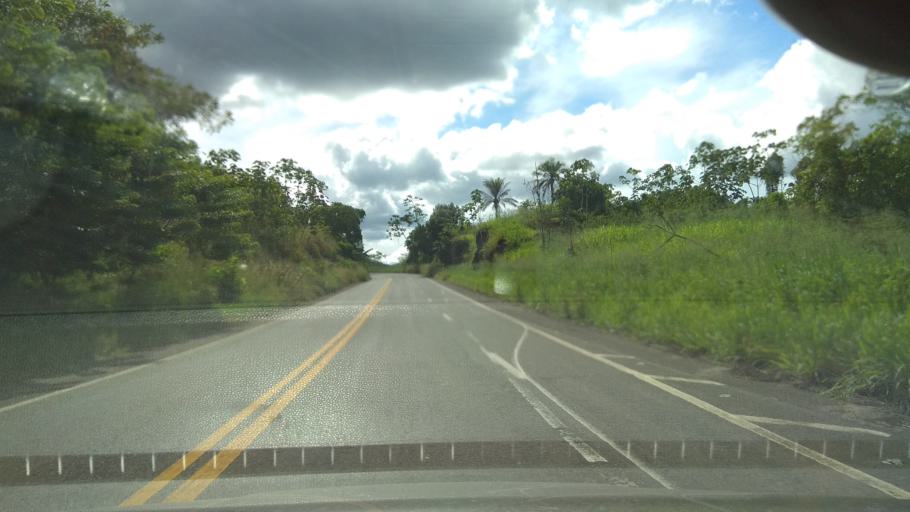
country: BR
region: Bahia
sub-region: Ubaitaba
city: Ubaitaba
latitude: -14.2481
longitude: -39.3582
